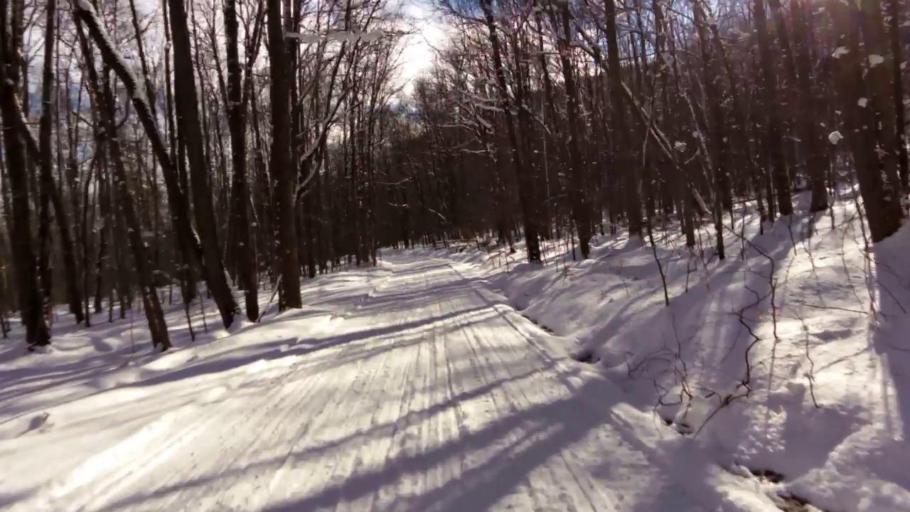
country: US
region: Pennsylvania
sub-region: McKean County
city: Foster Brook
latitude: 42.0667
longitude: -78.6621
